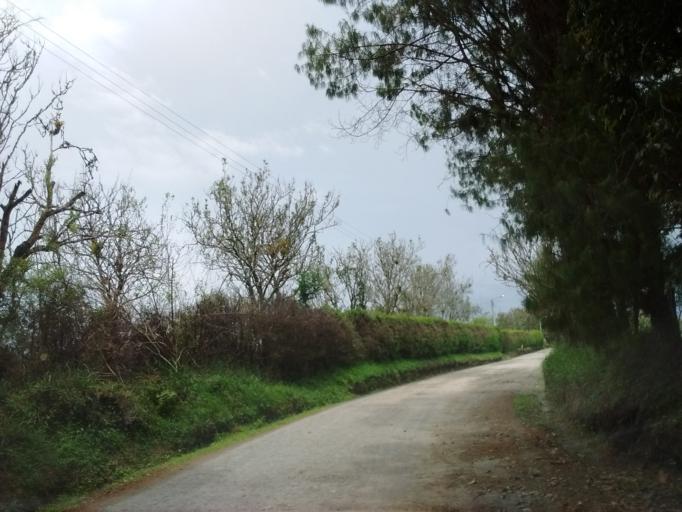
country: CO
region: Cauca
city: Cajibio
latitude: 2.5444
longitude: -76.6215
